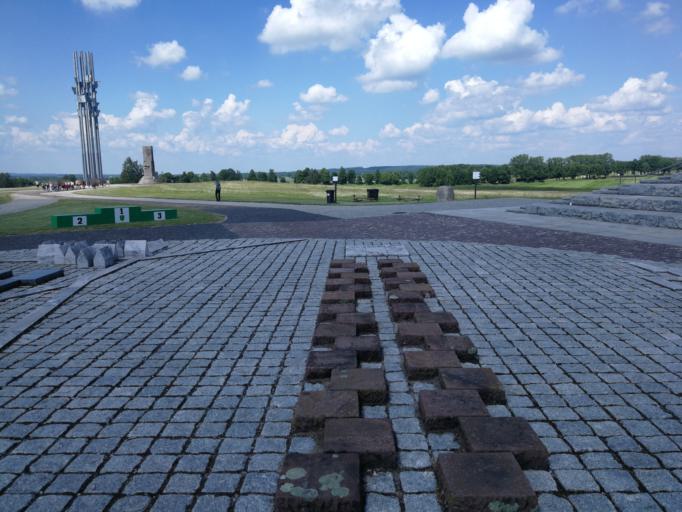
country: PL
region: Warmian-Masurian Voivodeship
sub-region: Powiat ostrodzki
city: Gierzwald
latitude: 53.4859
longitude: 20.1249
